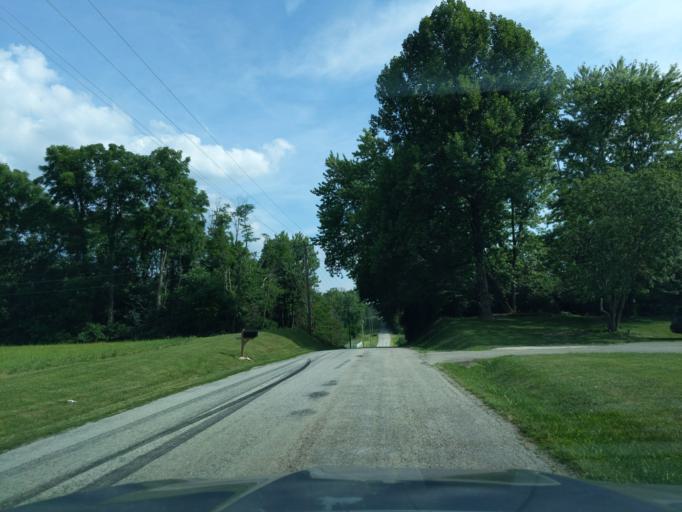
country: US
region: Indiana
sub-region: Decatur County
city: Greensburg
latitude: 39.2996
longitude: -85.4701
